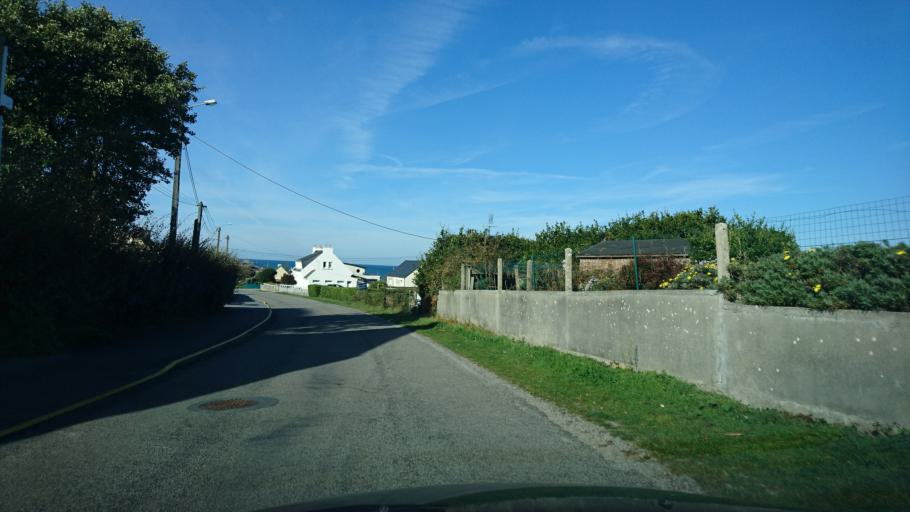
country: FR
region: Brittany
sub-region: Departement du Finistere
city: Lampaul-Plouarzel
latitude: 48.4363
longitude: -4.7752
